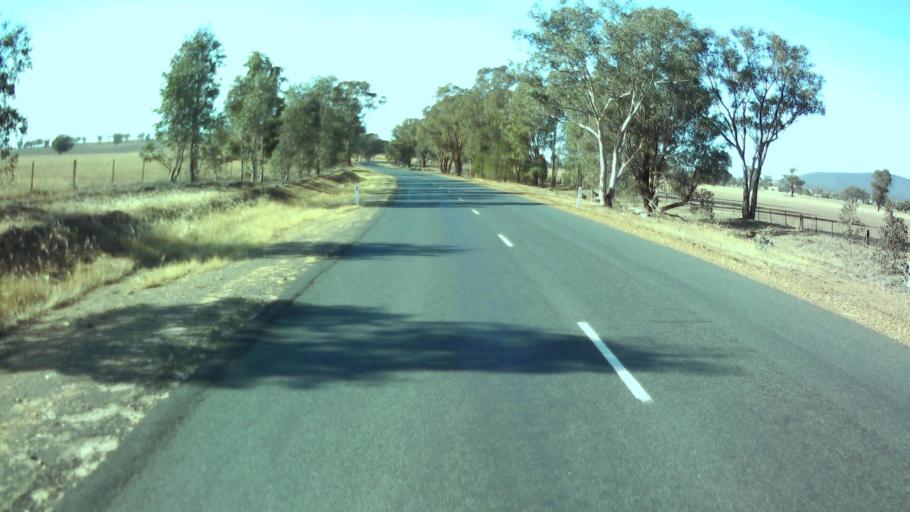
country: AU
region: New South Wales
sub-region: Weddin
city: Grenfell
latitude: -33.9308
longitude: 148.1374
